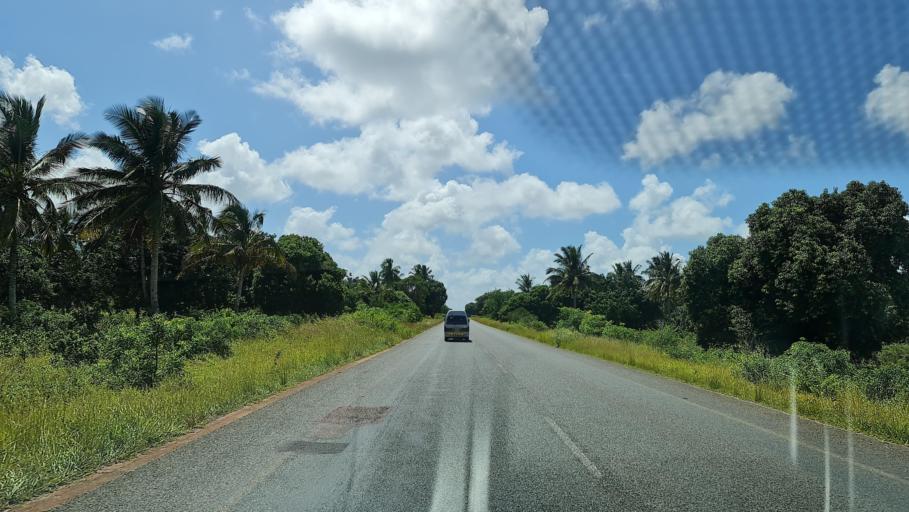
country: MZ
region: Inhambane
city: Maxixe
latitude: -24.5413
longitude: 34.9142
